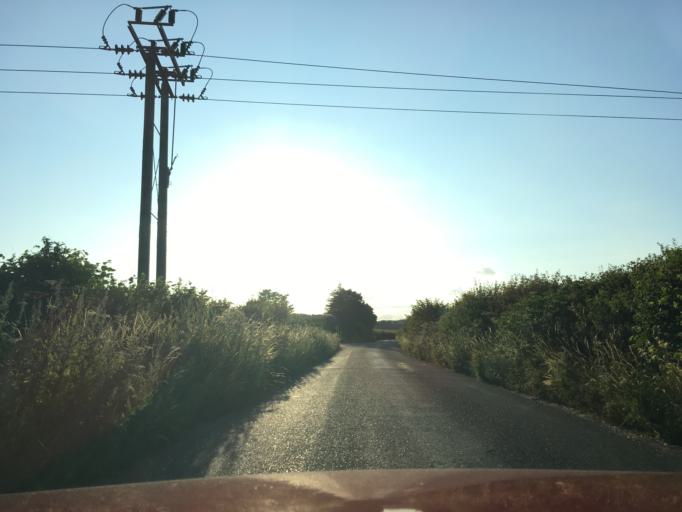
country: GB
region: England
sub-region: West Berkshire
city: Cold Ash
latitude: 51.4348
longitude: -1.2180
